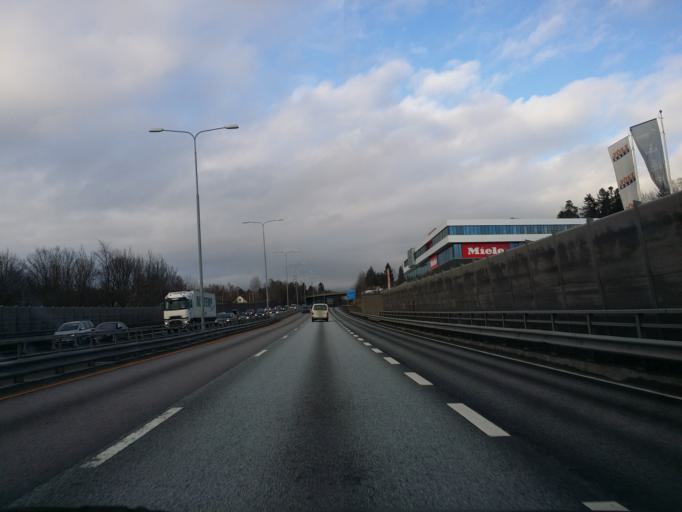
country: NO
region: Akershus
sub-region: Asker
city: Billingstad
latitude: 59.8668
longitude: 10.4890
